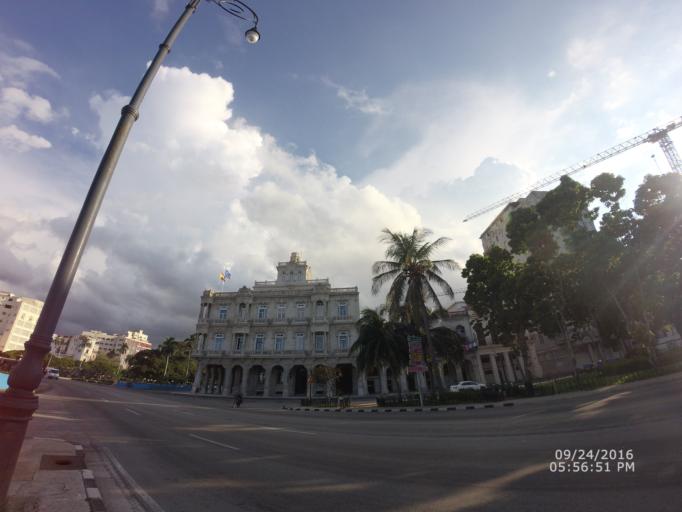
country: CU
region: La Habana
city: Centro Habana
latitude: 23.1443
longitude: -82.3570
